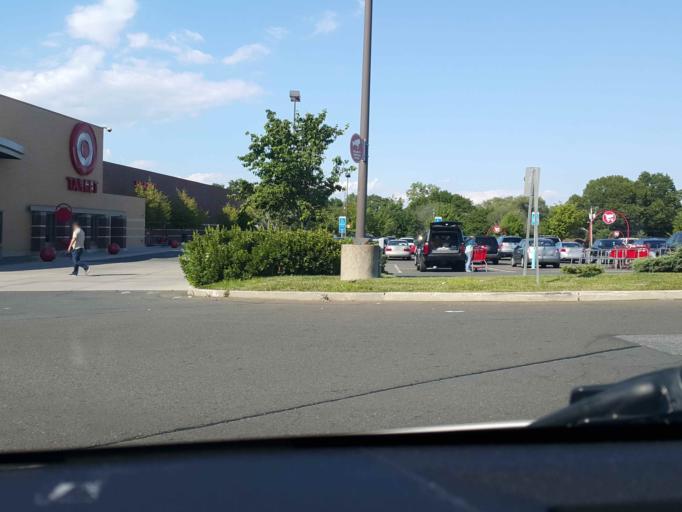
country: US
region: Connecticut
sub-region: New Haven County
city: Orange
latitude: 41.2798
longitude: -72.9877
